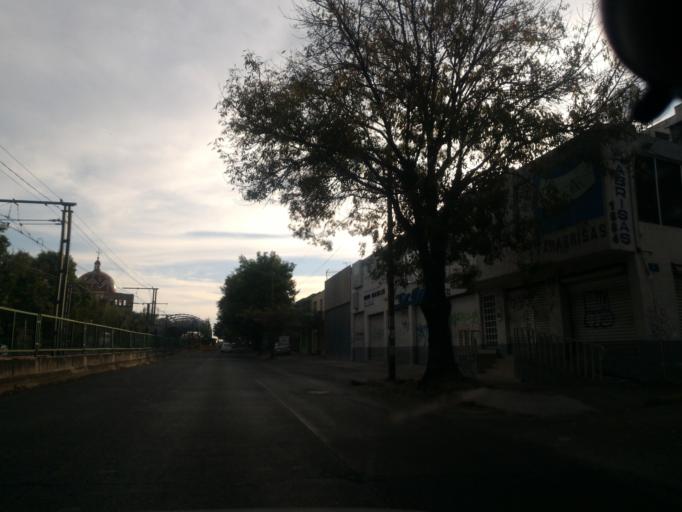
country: MX
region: Jalisco
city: Guadalajara
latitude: 20.6560
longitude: -103.3625
